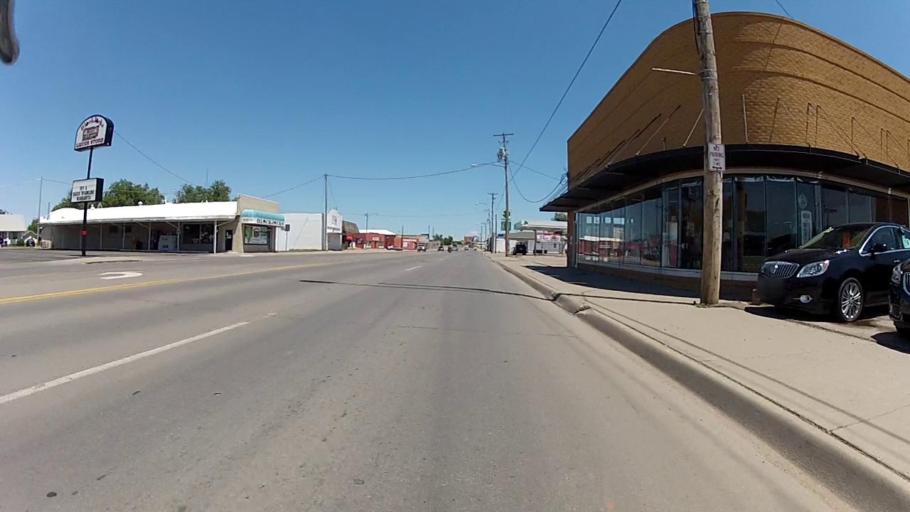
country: US
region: Kansas
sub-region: Ford County
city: Dodge City
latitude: 37.7439
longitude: -100.0194
